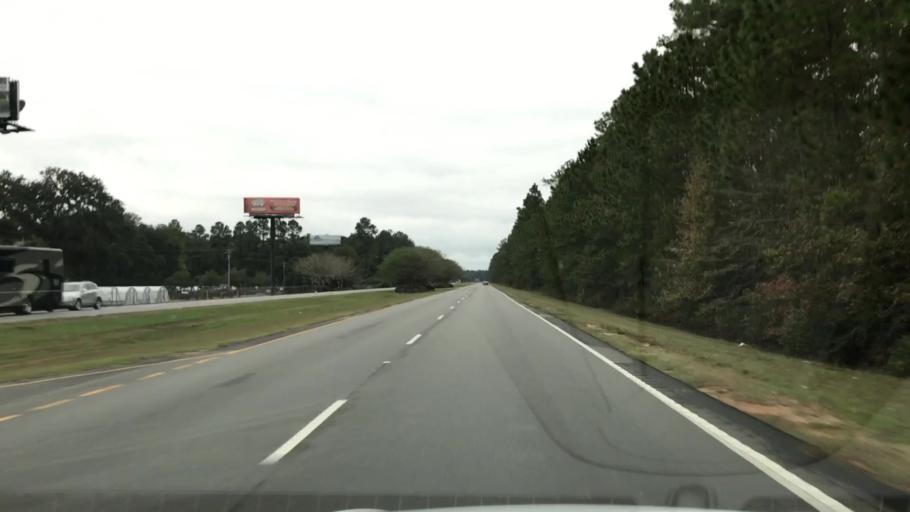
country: US
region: South Carolina
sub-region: Georgetown County
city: Georgetown
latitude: 33.2347
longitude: -79.3759
